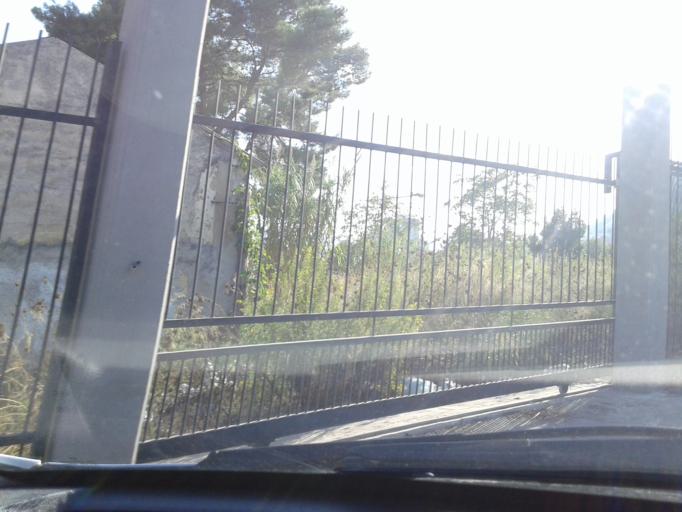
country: IT
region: Sicily
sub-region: Palermo
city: Monreale
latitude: 38.1005
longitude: 13.3163
